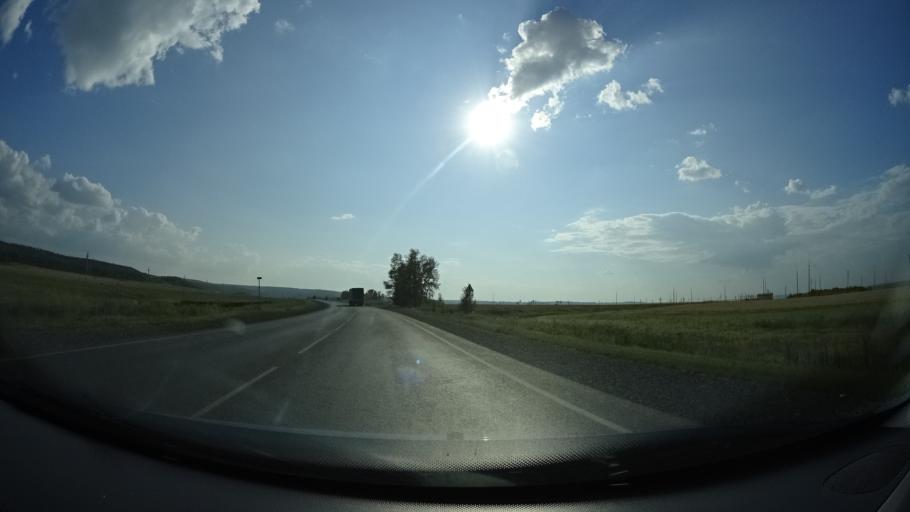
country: RU
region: Tatarstan
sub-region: Bavlinskiy Rayon
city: Bavly
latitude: 54.4739
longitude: 53.3151
